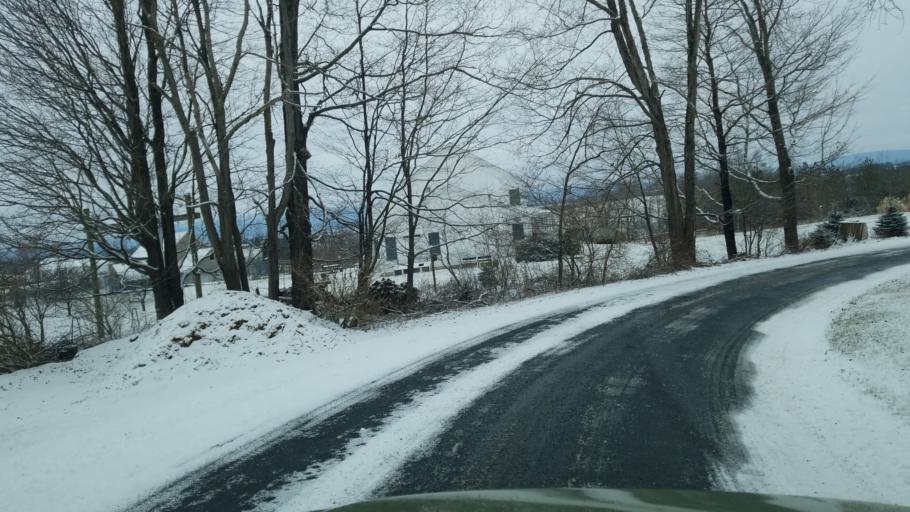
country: US
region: Pennsylvania
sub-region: Centre County
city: Centre Hall
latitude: 40.7743
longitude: -77.6708
